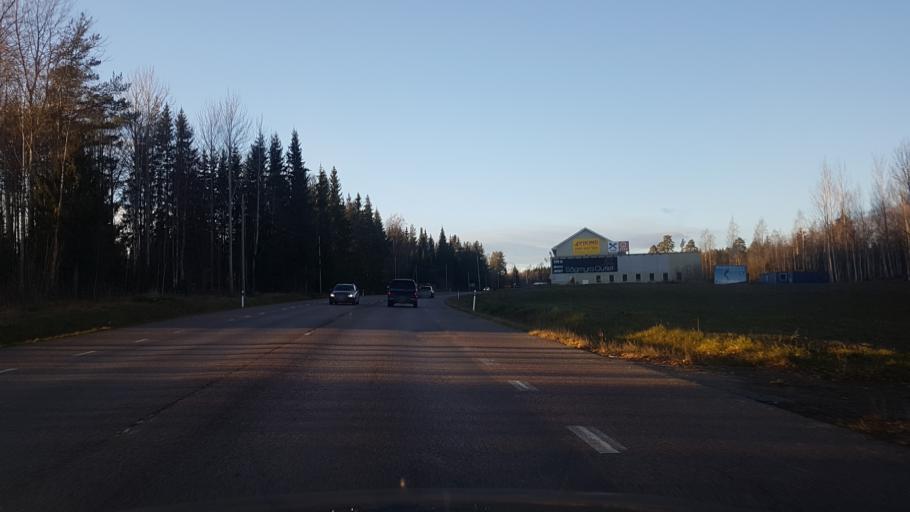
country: SE
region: Dalarna
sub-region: Faluns Kommun
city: Bjursas
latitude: 60.7207
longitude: 15.4532
